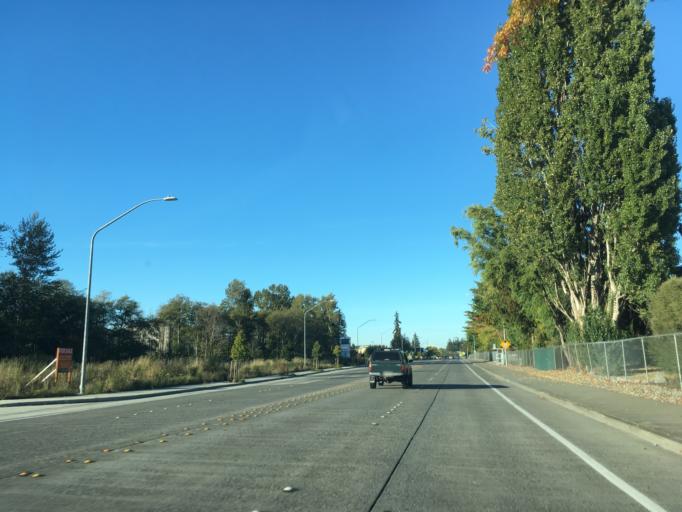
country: US
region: Washington
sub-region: Whatcom County
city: Bellingham
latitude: 48.7387
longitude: -122.4648
